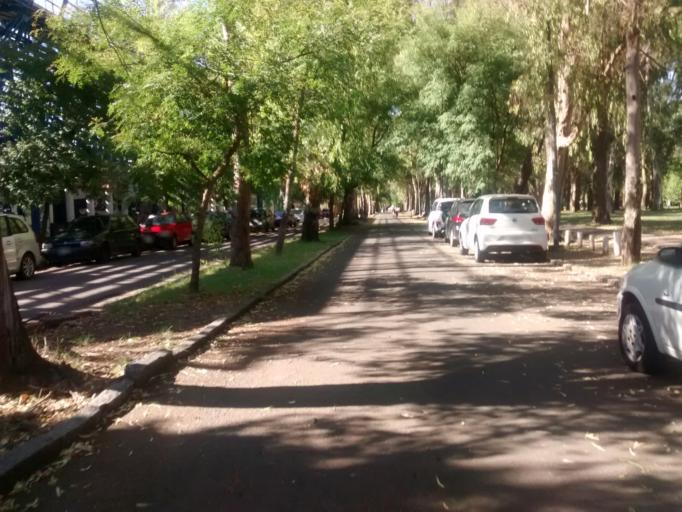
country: AR
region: Buenos Aires
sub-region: Partido de La Plata
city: La Plata
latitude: -34.9105
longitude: -57.9335
